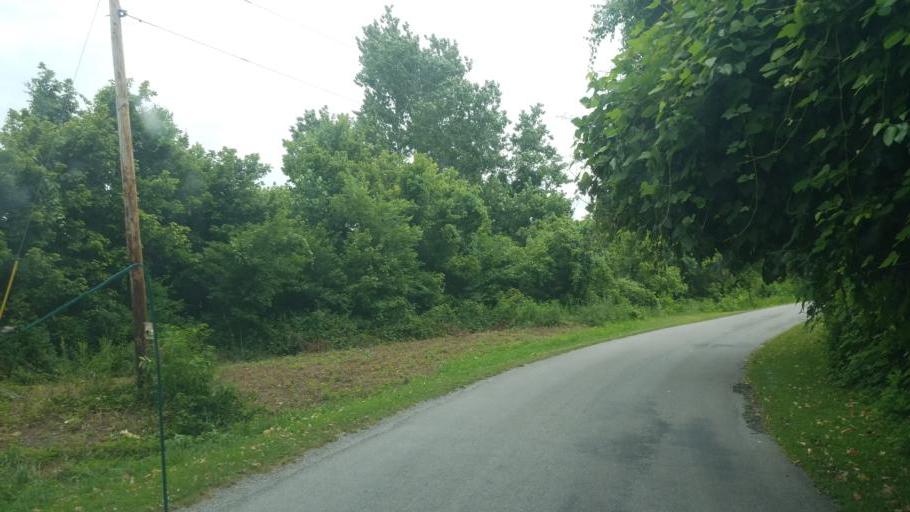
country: US
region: Illinois
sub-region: Jackson County
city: Murphysboro
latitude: 37.6740
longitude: -89.3902
